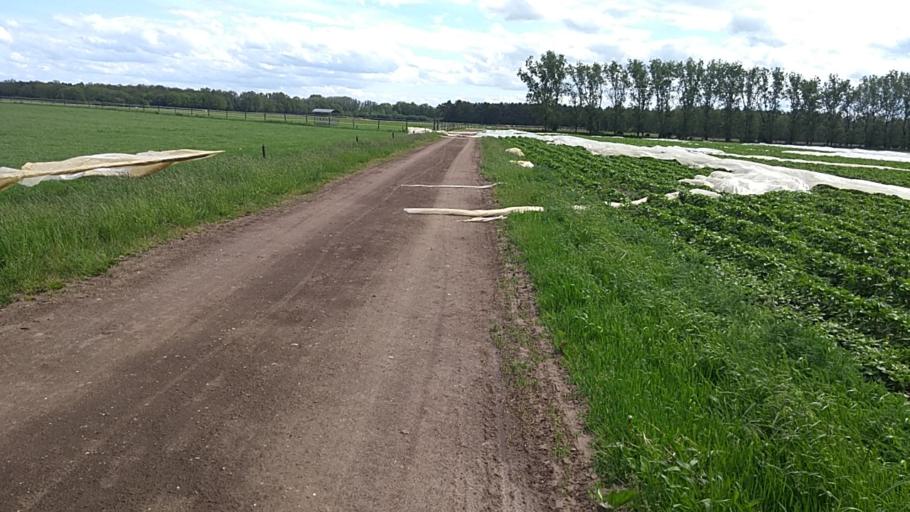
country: NL
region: Limburg
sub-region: Gemeente Leudal
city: Heythuysen
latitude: 51.3021
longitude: 5.8465
